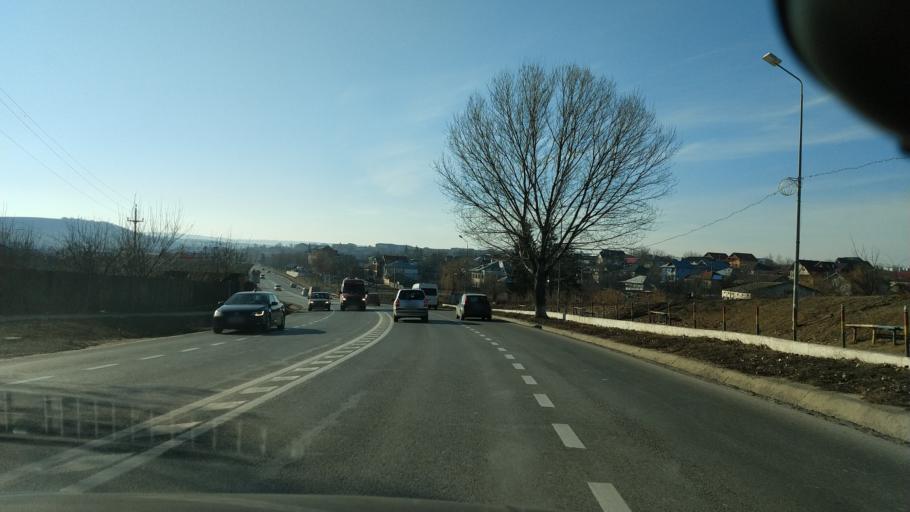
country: RO
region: Iasi
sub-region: Comuna Ion Neculce
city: Razboieni
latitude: 47.2170
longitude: 27.0312
